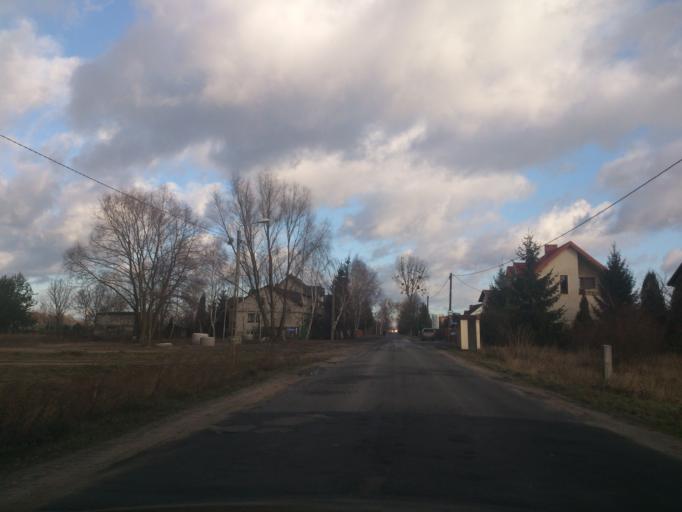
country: PL
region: Kujawsko-Pomorskie
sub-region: Powiat torunski
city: Lubicz Gorny
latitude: 53.0263
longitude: 18.8158
